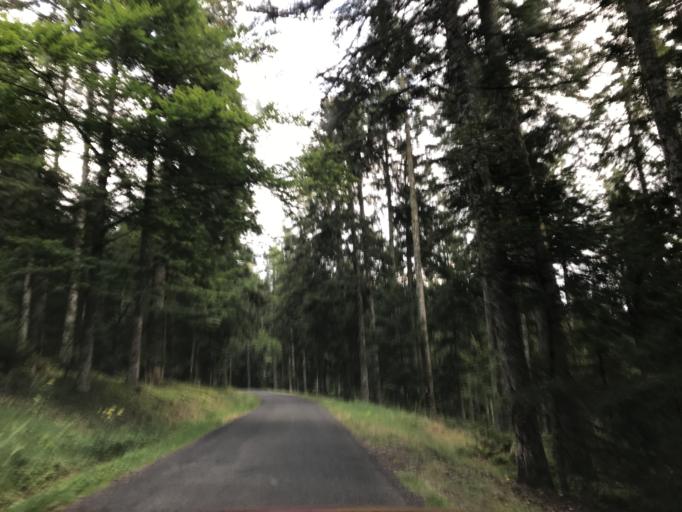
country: FR
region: Rhone-Alpes
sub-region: Departement de la Loire
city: Noiretable
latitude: 45.7659
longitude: 3.7263
